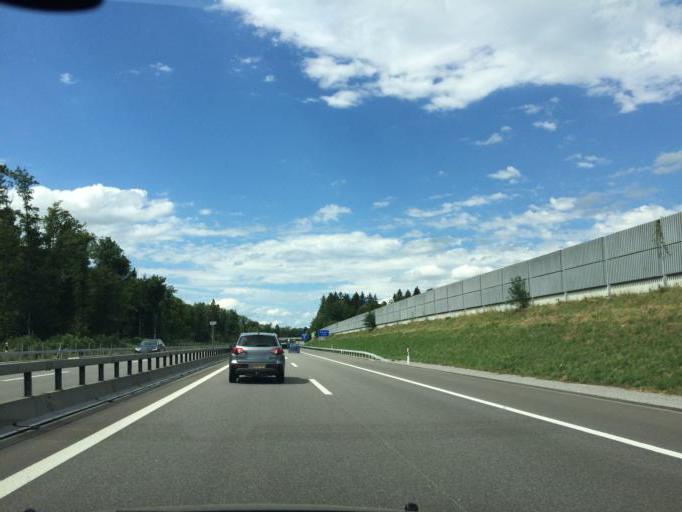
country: CH
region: Bern
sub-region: Bern-Mittelland District
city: Munsingen
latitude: 46.8713
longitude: 7.5459
